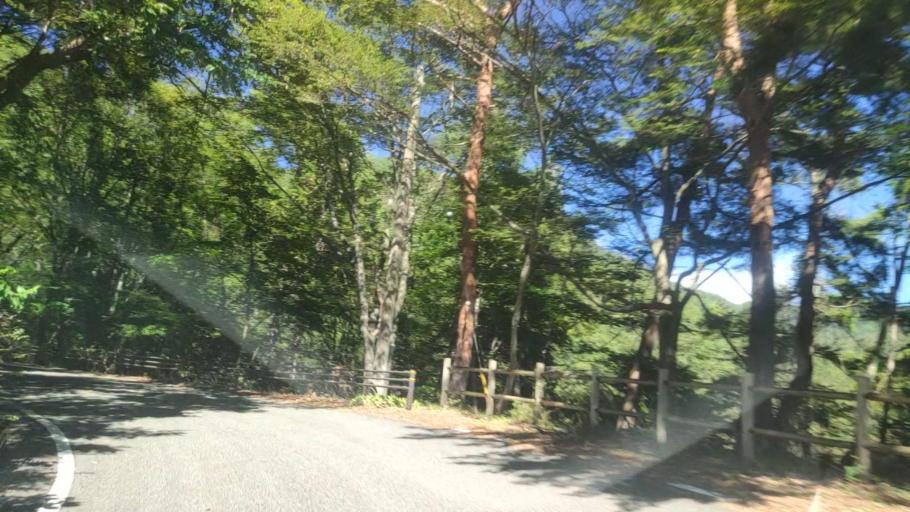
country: JP
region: Yamanashi
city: Fujikawaguchiko
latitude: 35.5477
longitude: 138.7743
